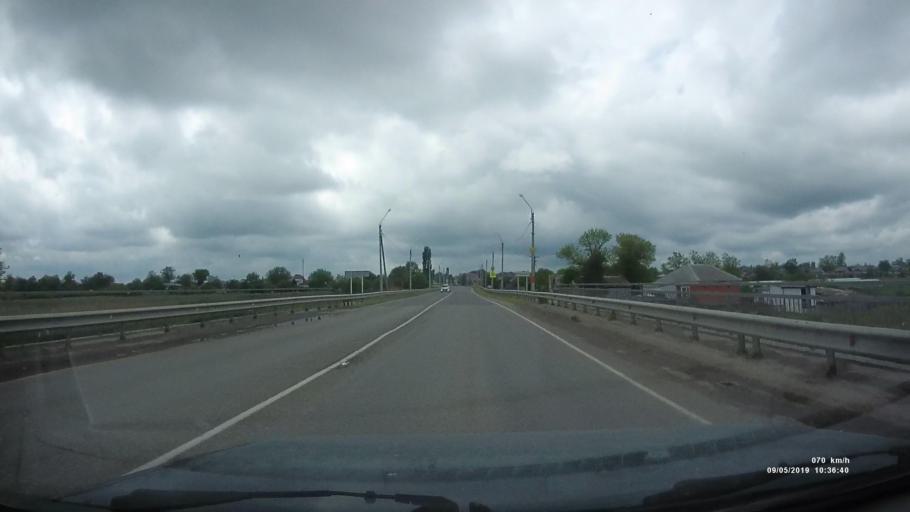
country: RU
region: Rostov
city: Peshkovo
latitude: 47.0269
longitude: 39.4067
